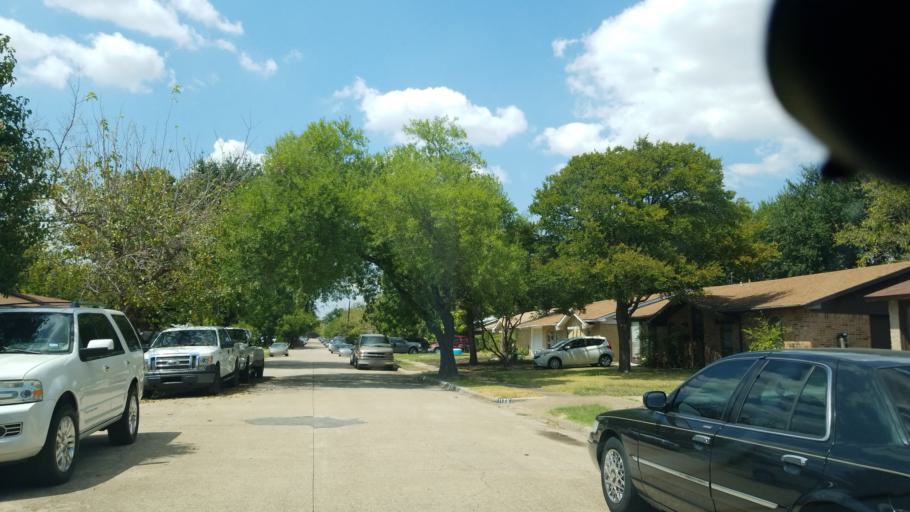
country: US
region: Texas
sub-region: Dallas County
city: Grand Prairie
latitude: 32.7055
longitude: -96.9892
